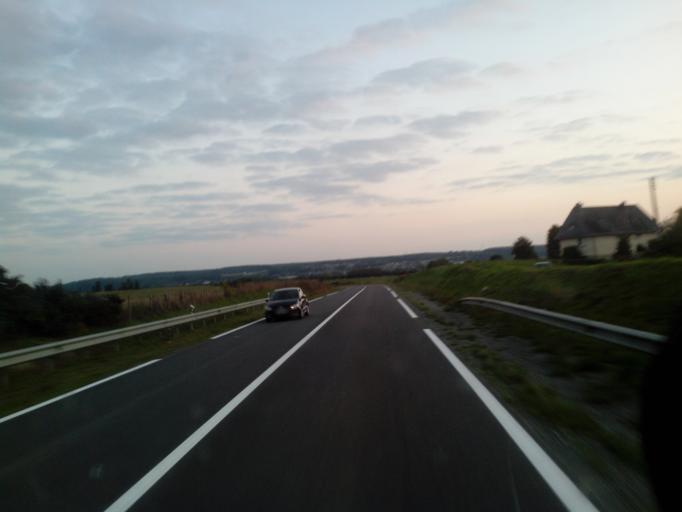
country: FR
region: Brittany
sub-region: Departement d'Ille-et-Vilaine
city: Bedee
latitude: 48.1584
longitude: -1.9460
